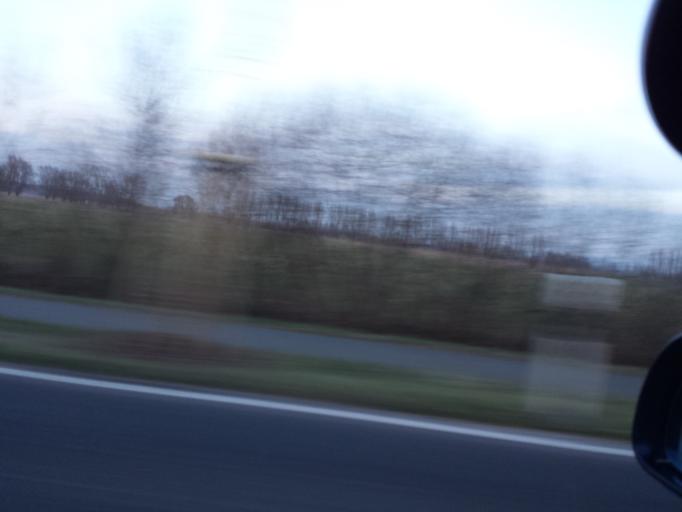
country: DE
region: Brandenburg
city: Kremmen
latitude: 52.7966
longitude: 13.0352
